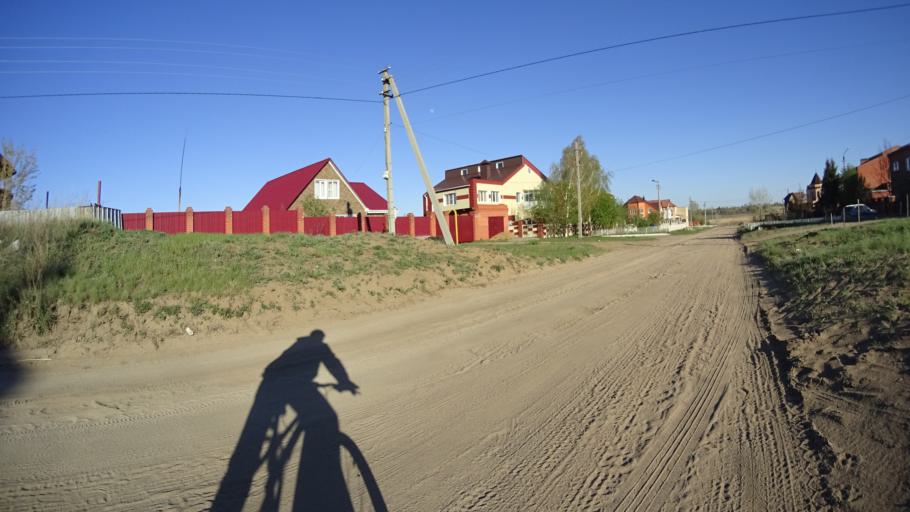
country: RU
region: Chelyabinsk
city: Troitsk
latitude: 54.0710
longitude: 61.5365
